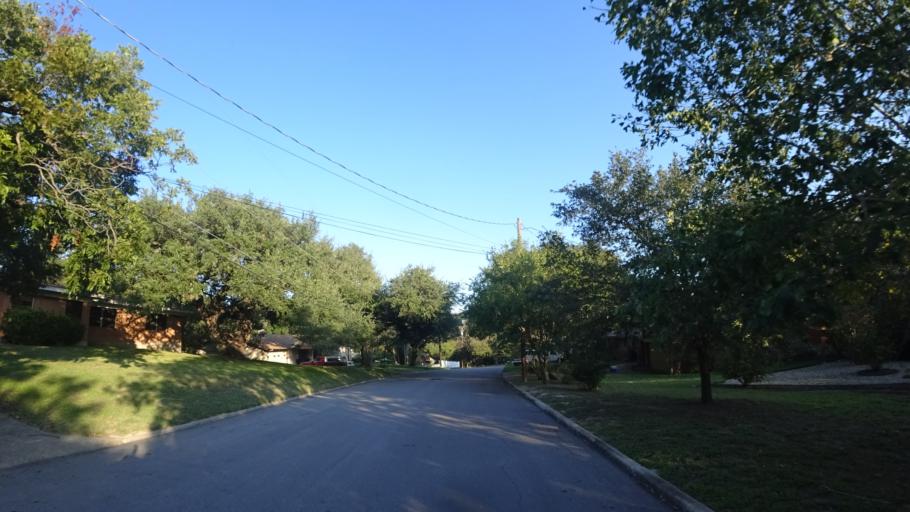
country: US
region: Texas
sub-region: Travis County
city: Wells Branch
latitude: 30.3632
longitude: -97.6738
